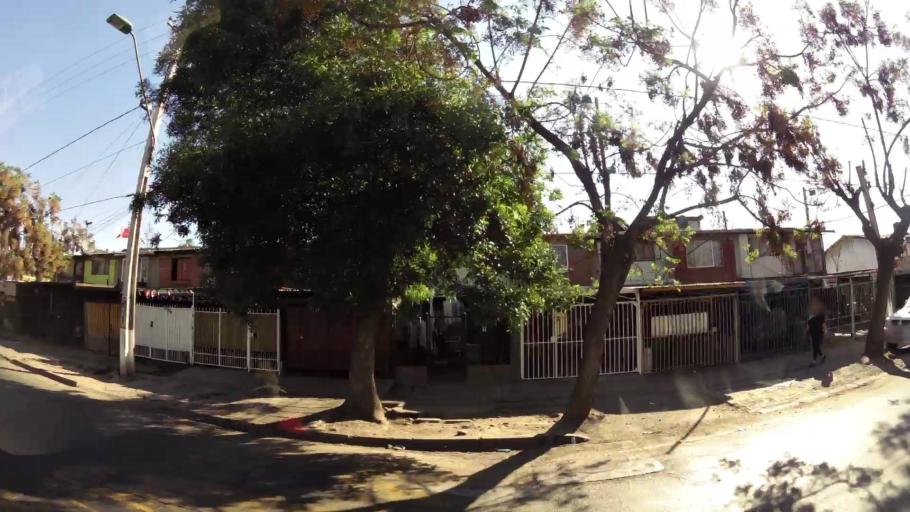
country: CL
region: Santiago Metropolitan
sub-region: Provincia de Santiago
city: La Pintana
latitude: -33.5612
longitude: -70.6107
